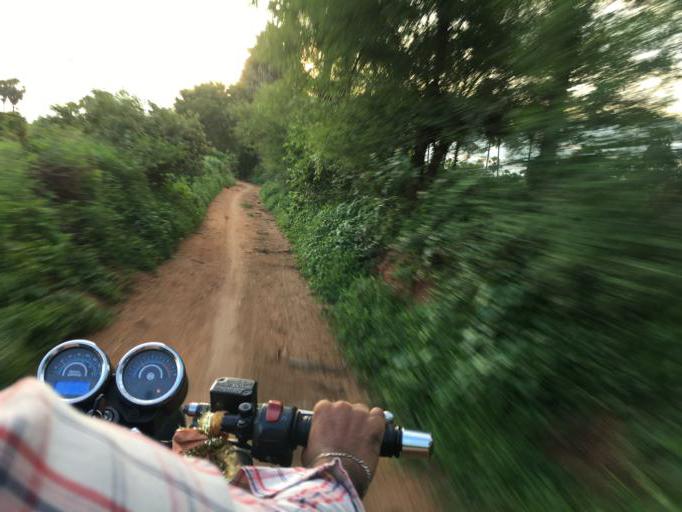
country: IN
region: Telangana
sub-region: Nalgonda
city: Nalgonda
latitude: 17.1762
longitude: 79.4144
